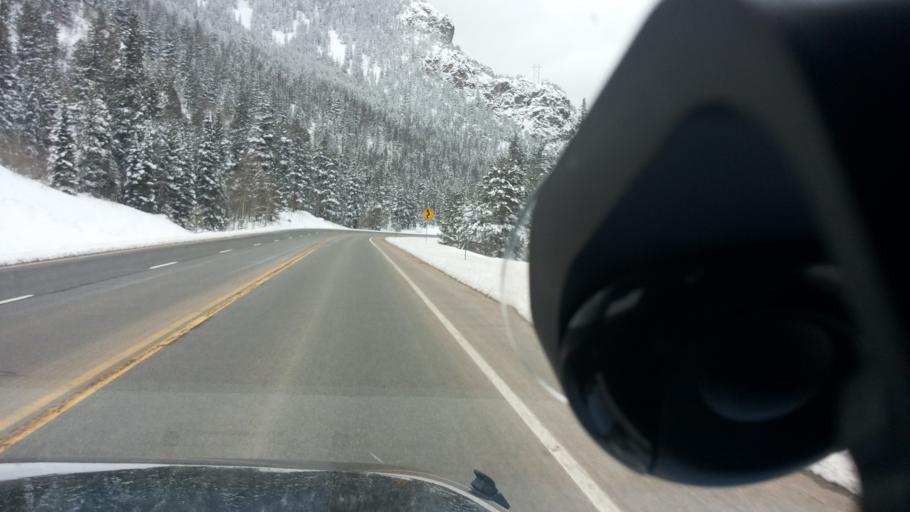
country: US
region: Colorado
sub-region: Clear Creek County
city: Georgetown
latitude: 39.7727
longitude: -105.7621
